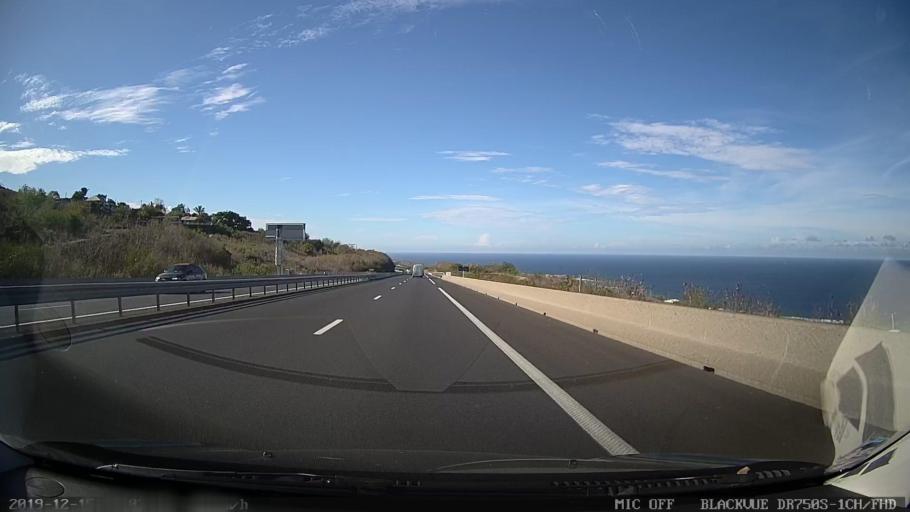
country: RE
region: Reunion
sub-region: Reunion
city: Saint-Leu
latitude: -21.1752
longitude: 55.2971
